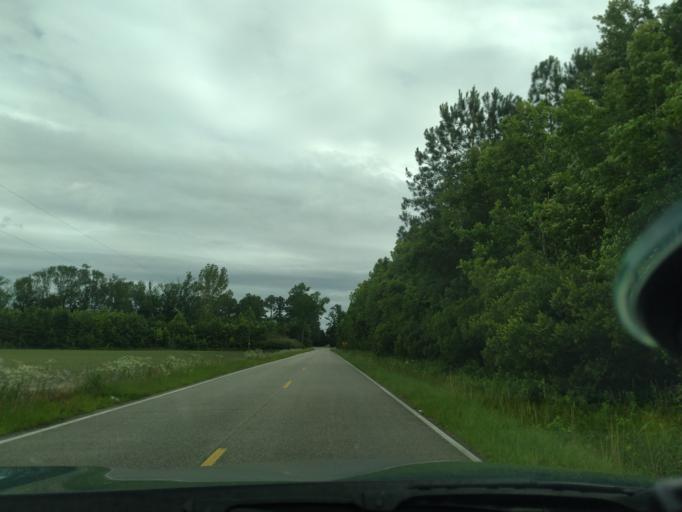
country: US
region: North Carolina
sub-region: Washington County
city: Plymouth
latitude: 35.8725
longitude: -76.7043
